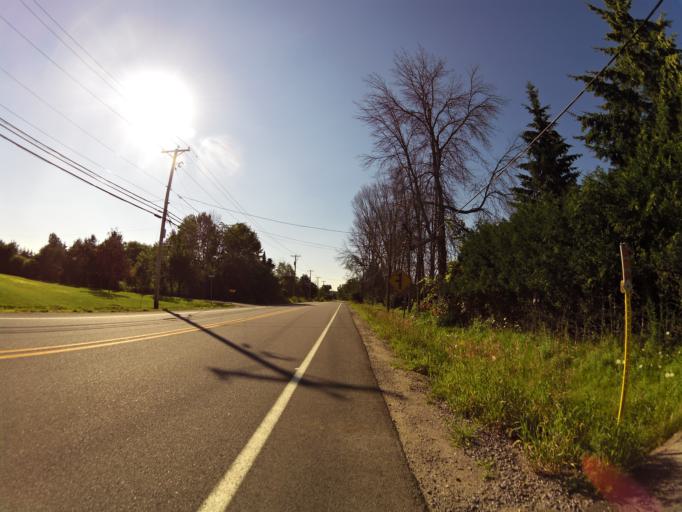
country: CA
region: Quebec
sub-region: Outaouais
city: Gatineau
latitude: 45.4939
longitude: -75.7723
